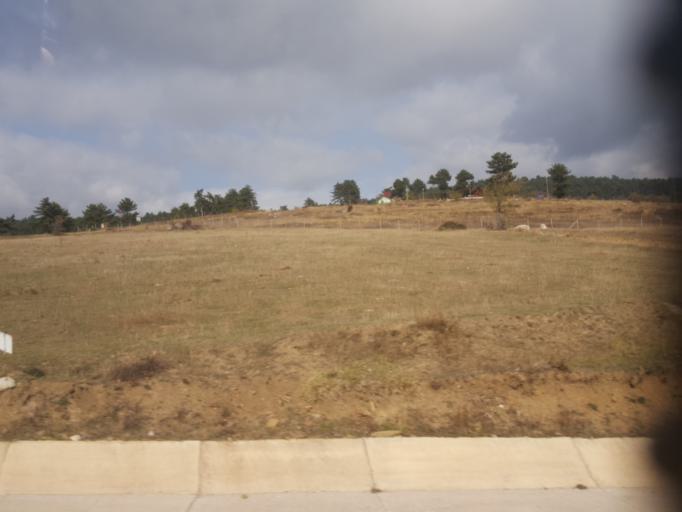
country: TR
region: Sinop
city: Duragan
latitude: 41.4970
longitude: 35.0347
